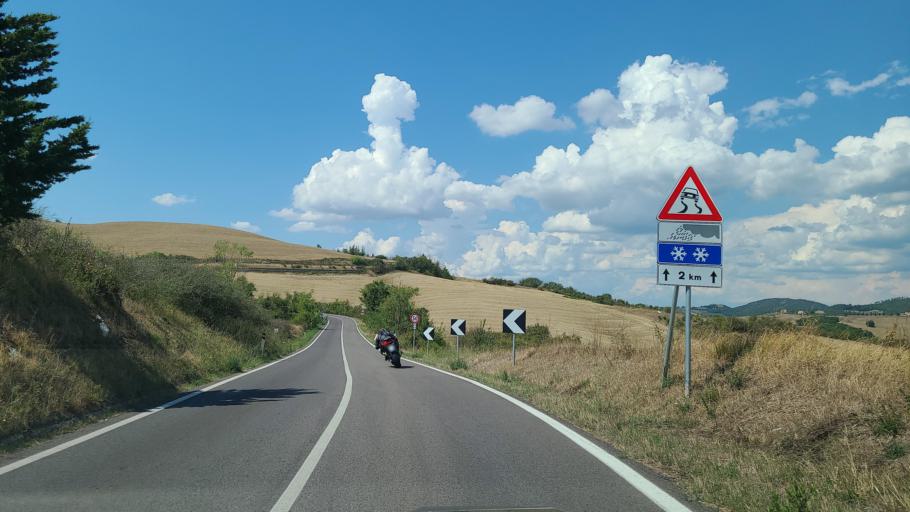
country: IT
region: Tuscany
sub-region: Province of Pisa
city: Volterra
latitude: 43.3843
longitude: 10.9228
